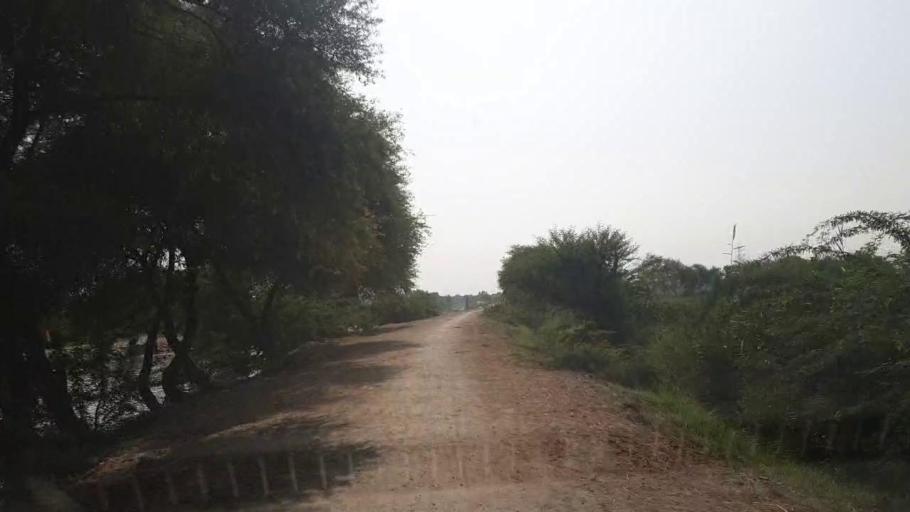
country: PK
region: Sindh
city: Badin
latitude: 24.6456
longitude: 68.8472
